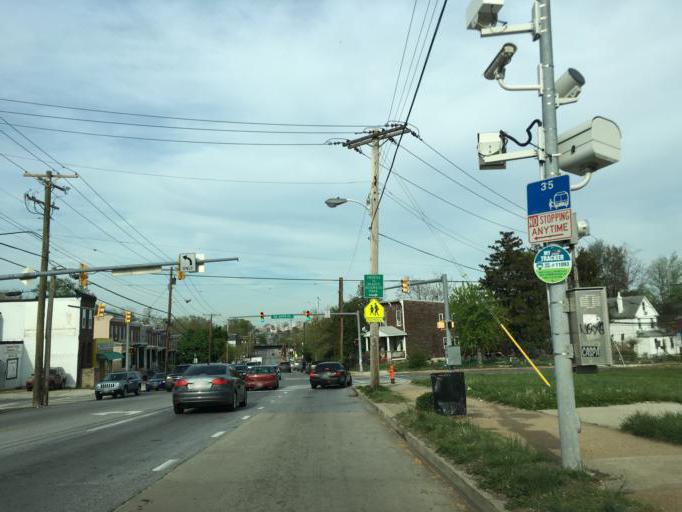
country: US
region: Maryland
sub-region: Baltimore County
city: Lansdowne
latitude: 39.2747
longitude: -76.6688
